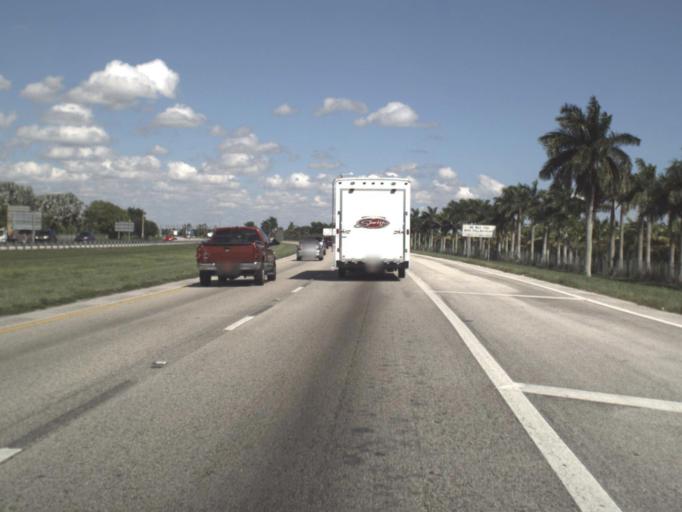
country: US
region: Florida
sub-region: Miami-Dade County
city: Goulds
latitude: 25.5416
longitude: -80.3634
